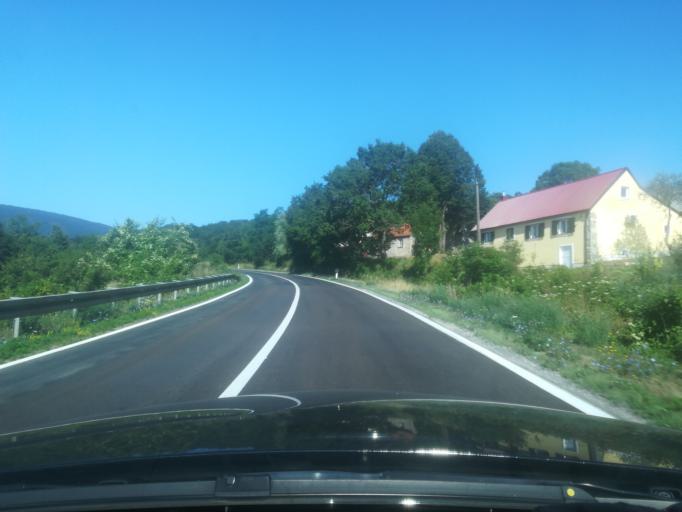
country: HR
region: Licko-Senjska
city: Brinje
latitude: 44.9685
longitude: 15.0600
